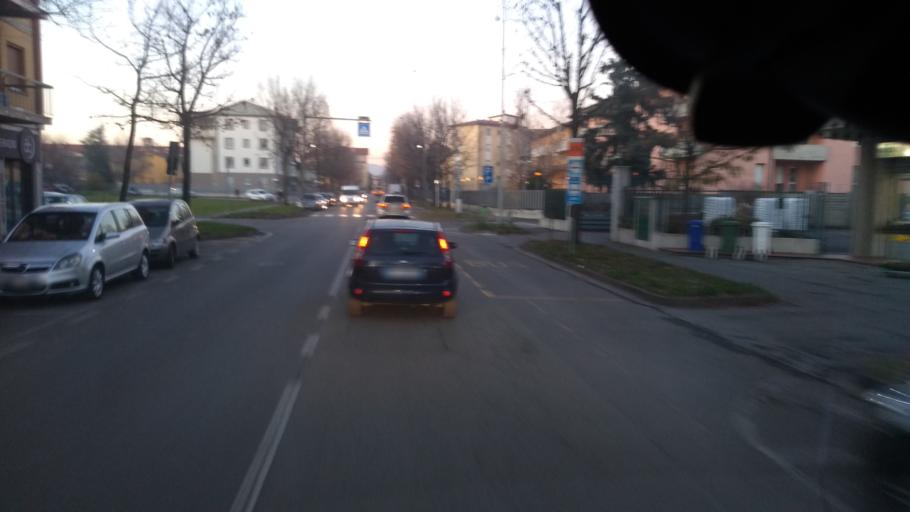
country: IT
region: Lombardy
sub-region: Provincia di Bergamo
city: Treviglio
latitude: 45.5224
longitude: 9.5997
